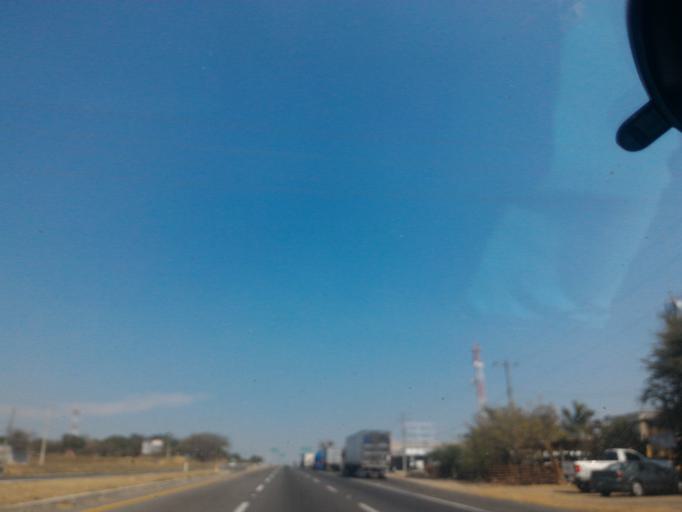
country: MX
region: Colima
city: Cuauhtemoc
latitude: 19.3094
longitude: -103.6079
